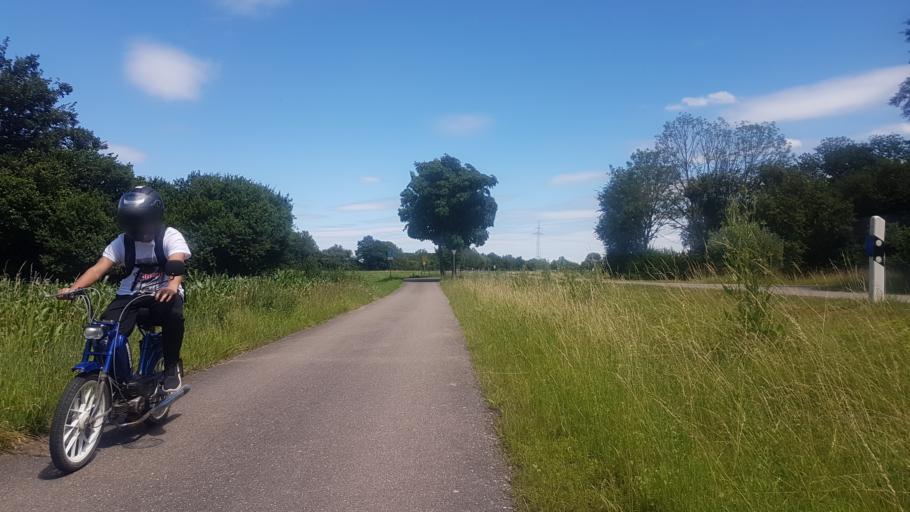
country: DE
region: Bavaria
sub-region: Swabia
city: Schwenningen
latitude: 48.6306
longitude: 10.6828
